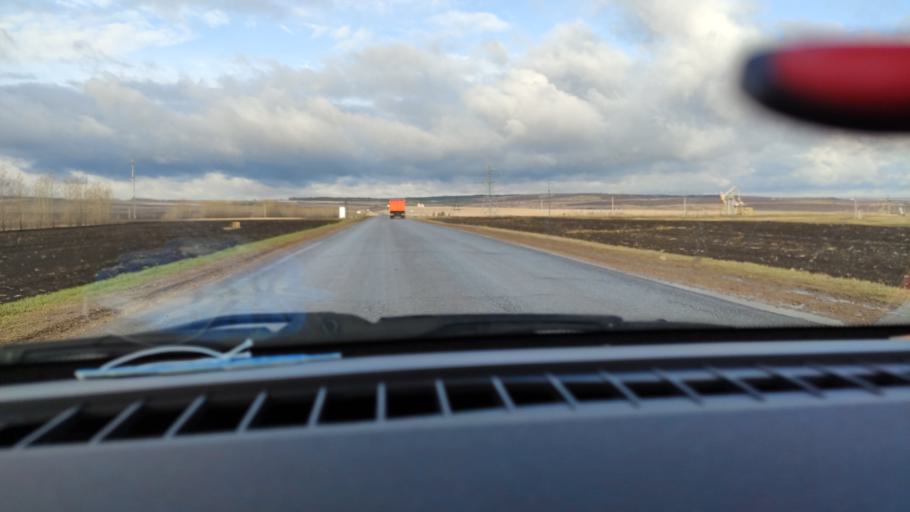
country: RU
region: Tatarstan
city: Russkiy Aktash
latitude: 55.0414
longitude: 52.0733
